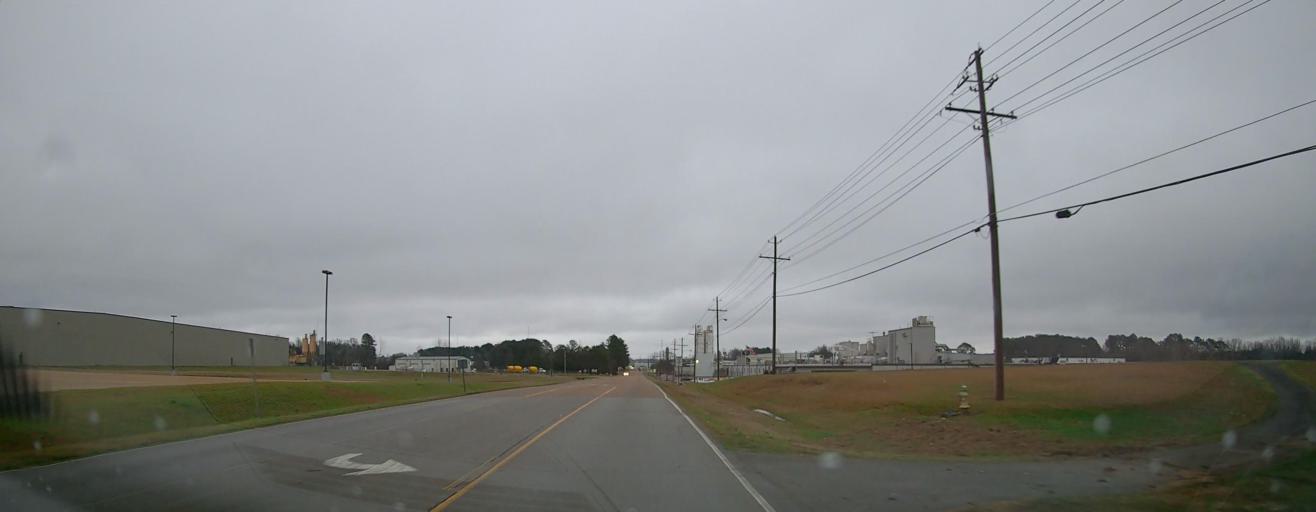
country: US
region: Mississippi
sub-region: Alcorn County
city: Corinth
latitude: 34.9088
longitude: -88.5317
